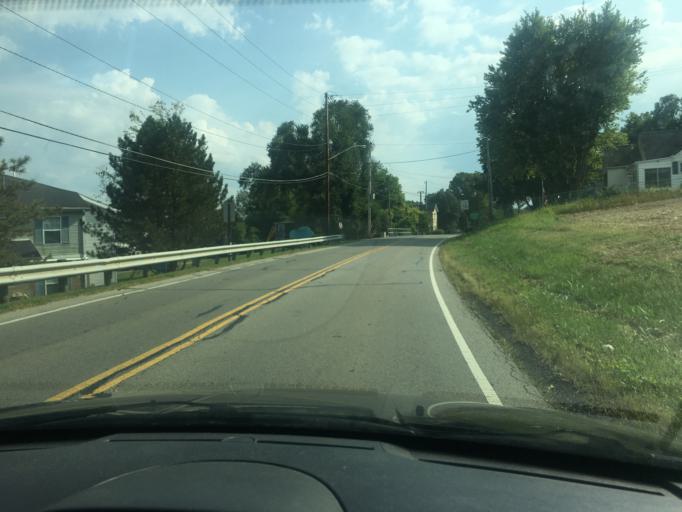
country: US
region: Ohio
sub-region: Champaign County
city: Urbana
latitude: 40.1192
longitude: -83.7643
